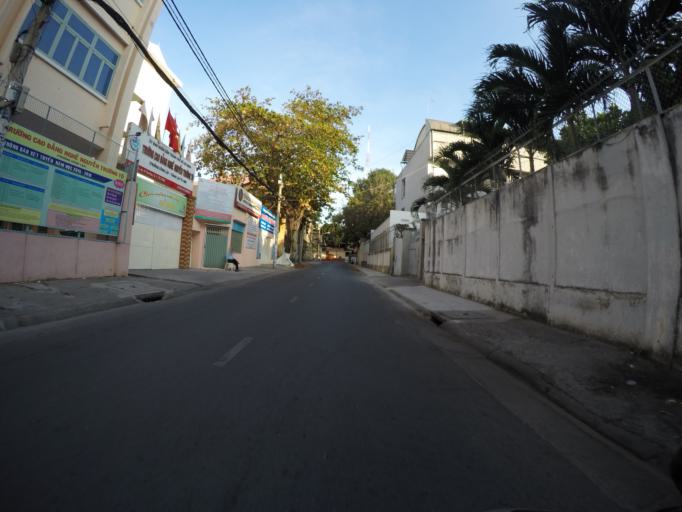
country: VN
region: Ho Chi Minh City
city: Quan Mot
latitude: 10.7902
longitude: 106.7002
